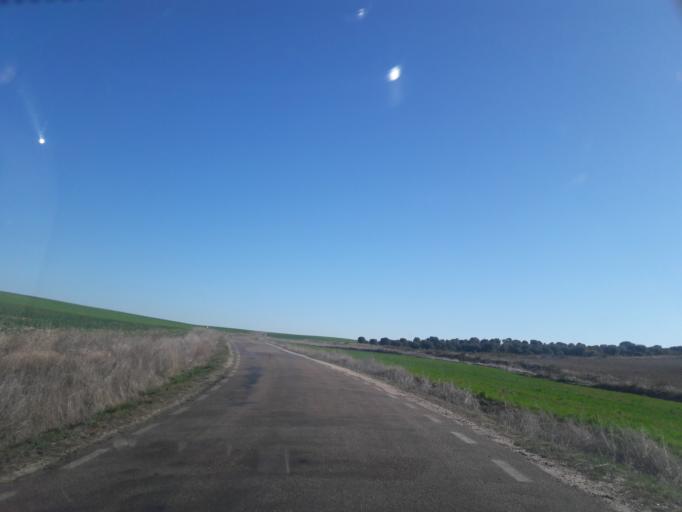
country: ES
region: Castille and Leon
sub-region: Provincia de Salamanca
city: Tordillos
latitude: 40.8640
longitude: -5.3380
